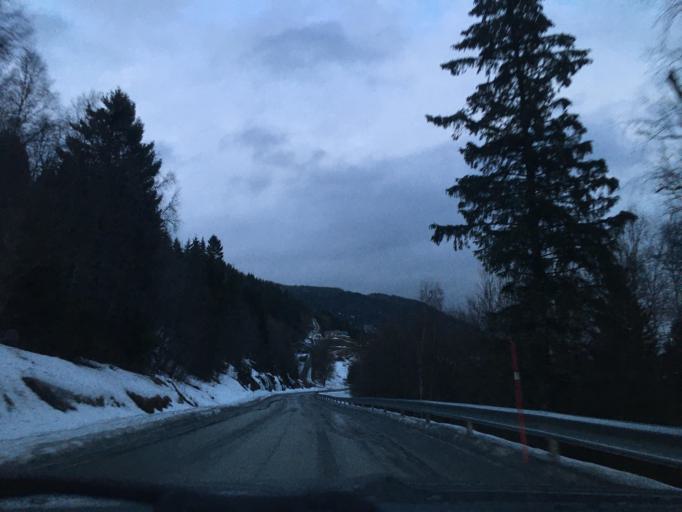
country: NO
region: Nordland
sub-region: Rana
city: Hauknes
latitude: 66.3066
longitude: 13.9716
